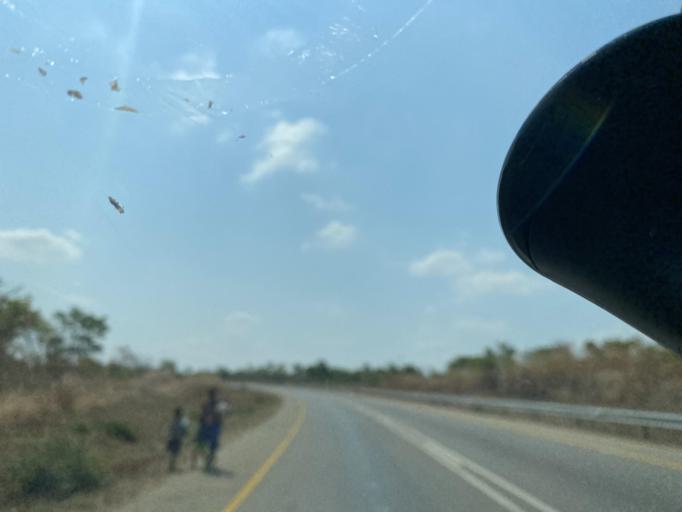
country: ZM
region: Lusaka
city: Chongwe
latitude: -15.5317
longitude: 28.6377
